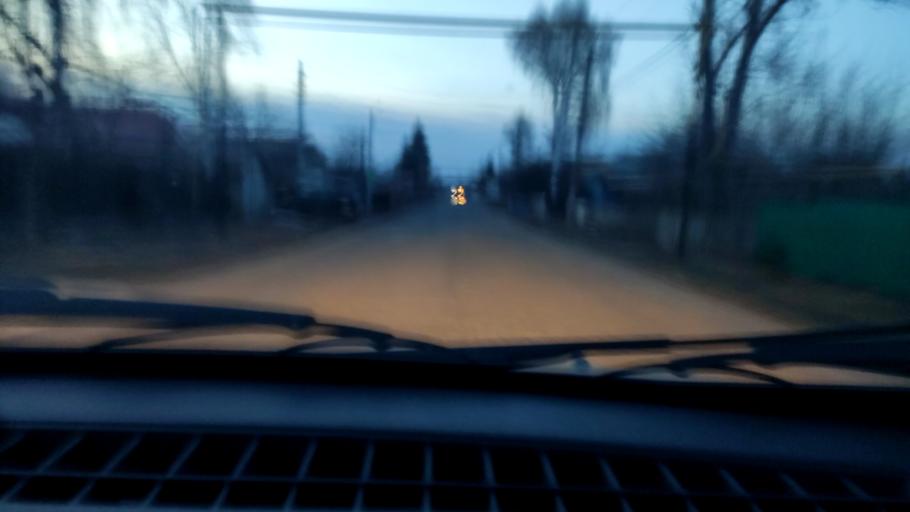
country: RU
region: Bashkortostan
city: Iglino
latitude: 54.8118
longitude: 56.3930
